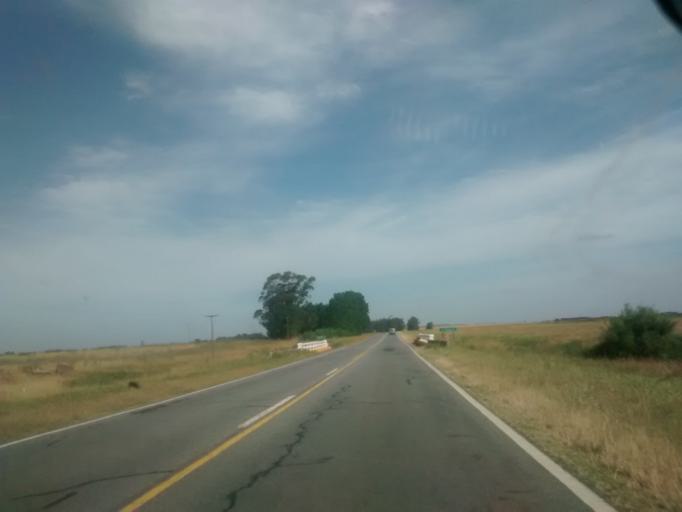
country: AR
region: Buenos Aires
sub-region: Partido de Balcarce
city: Balcarce
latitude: -37.6609
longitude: -58.5546
